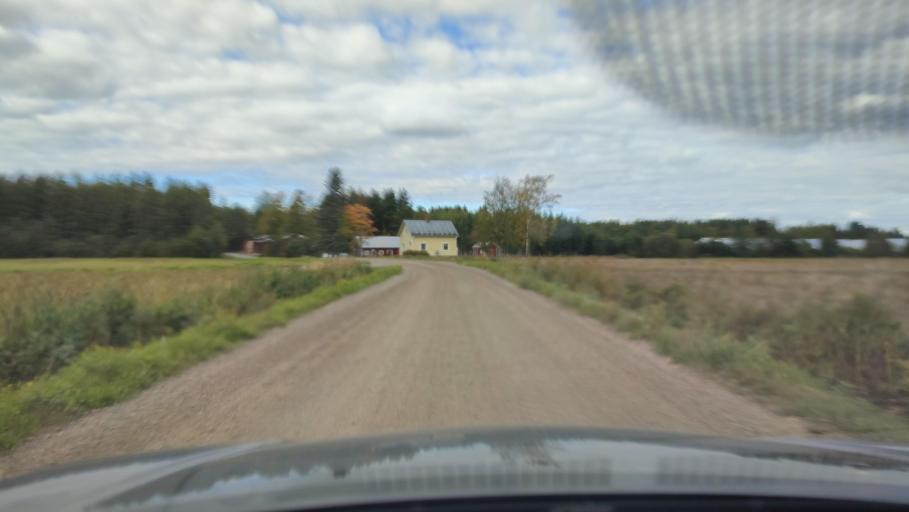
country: FI
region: Southern Ostrobothnia
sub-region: Suupohja
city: Karijoki
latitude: 62.2355
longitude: 21.6029
